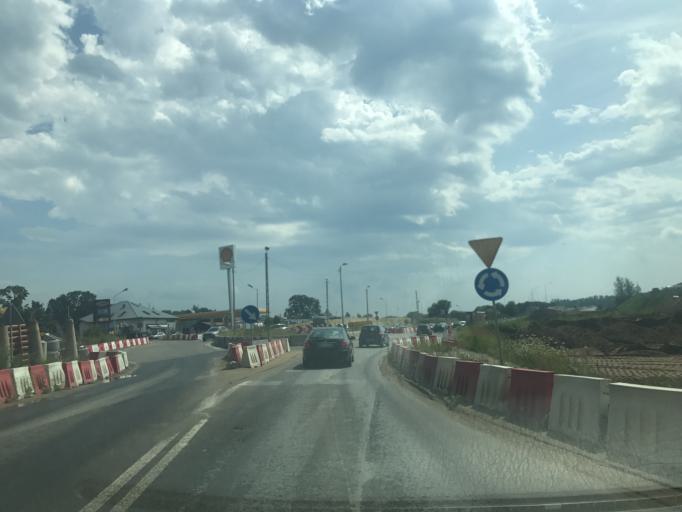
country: PL
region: Warmian-Masurian Voivodeship
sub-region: Powiat ostrodzki
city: Ostroda
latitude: 53.7101
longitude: 19.9769
